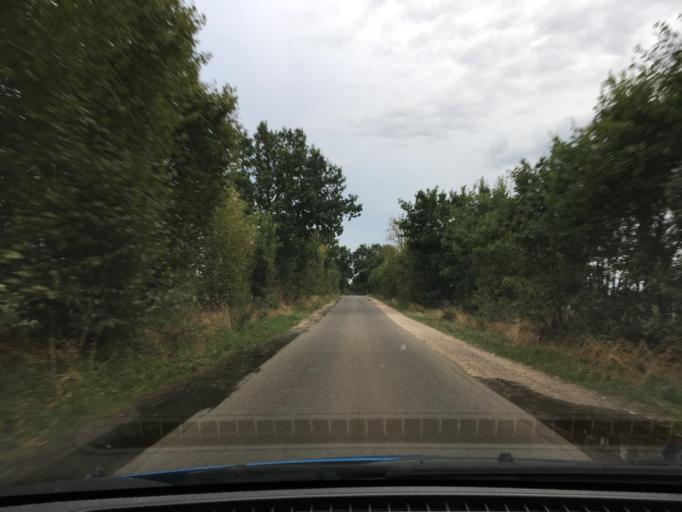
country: DE
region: Schleswig-Holstein
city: Lanze
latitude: 53.4079
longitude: 10.6066
